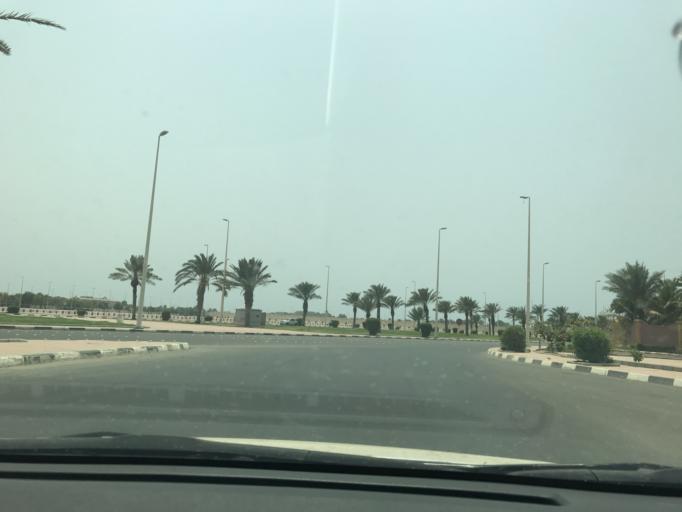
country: SA
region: Makkah
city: Jeddah
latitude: 21.6830
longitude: 39.1055
